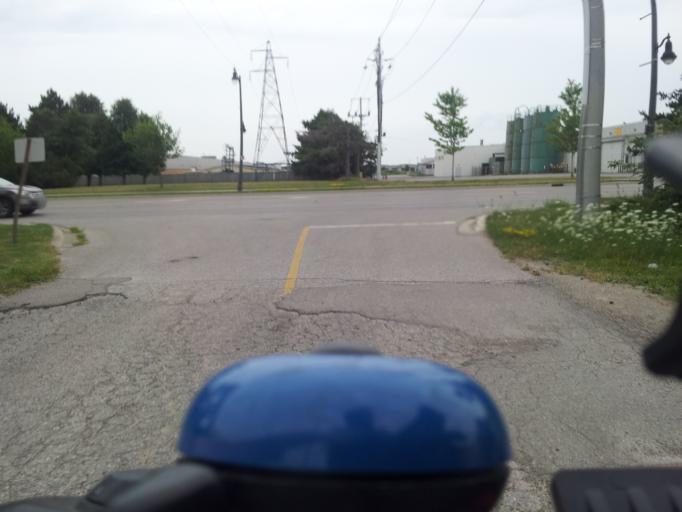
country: CA
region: Ontario
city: Stratford
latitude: 43.3713
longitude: -80.9555
